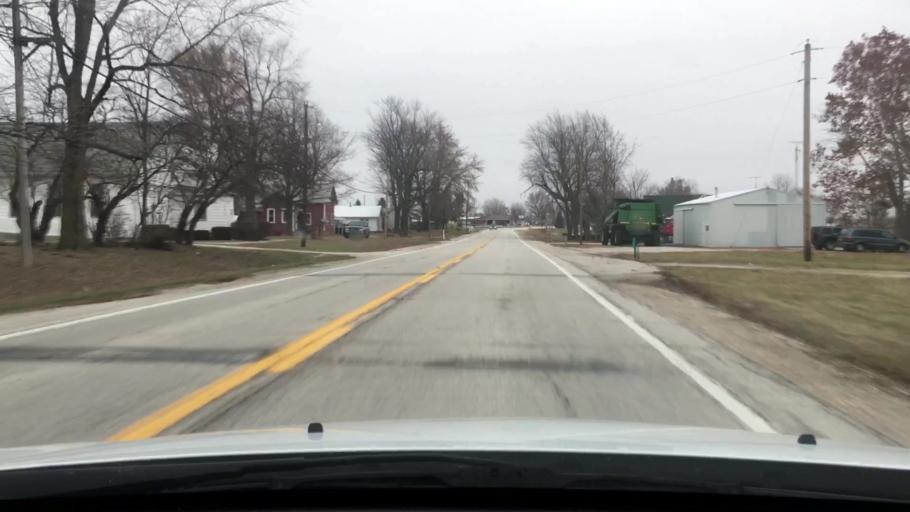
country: US
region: Illinois
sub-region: Pike County
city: Pittsfield
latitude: 39.5731
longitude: -90.9123
